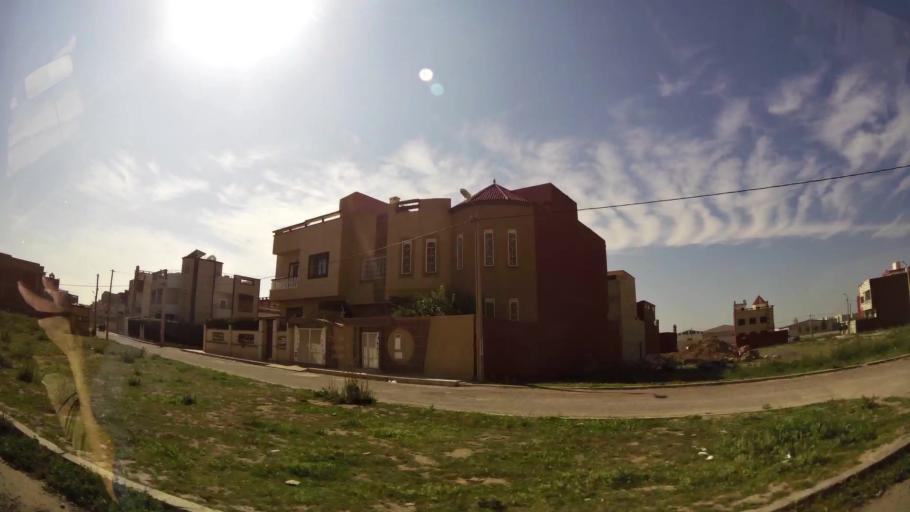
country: MA
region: Oriental
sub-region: Oujda-Angad
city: Oujda
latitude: 34.6985
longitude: -1.8808
